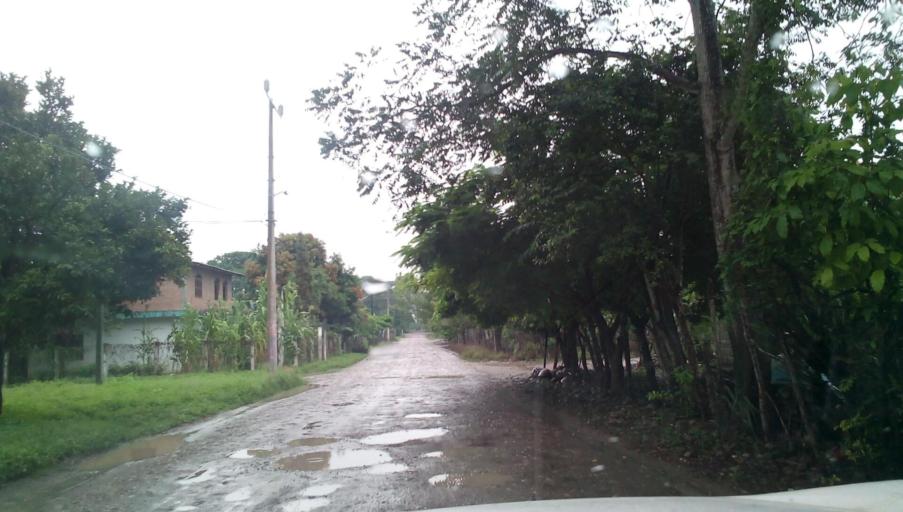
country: MX
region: Veracruz
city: Tempoal de Sanchez
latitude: 21.4175
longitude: -98.4279
